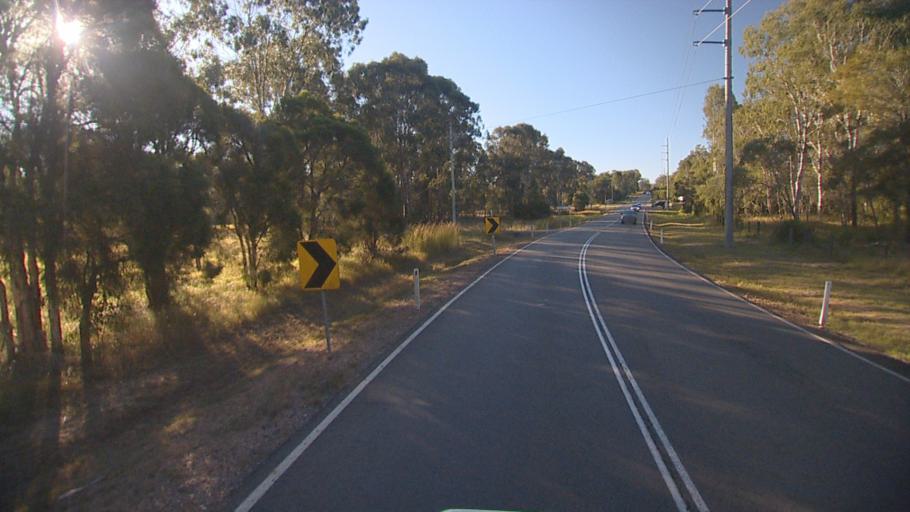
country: AU
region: Queensland
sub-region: Logan
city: Chambers Flat
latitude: -27.7404
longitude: 153.0869
